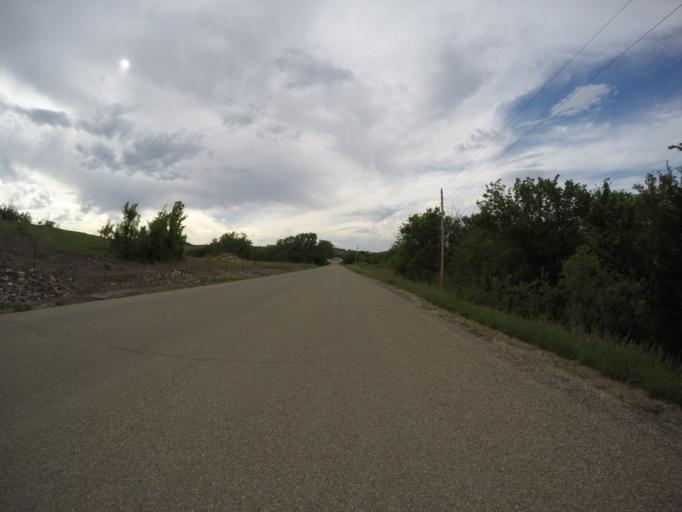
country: US
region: Kansas
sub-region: Riley County
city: Ogden
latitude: 39.0415
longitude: -96.6322
